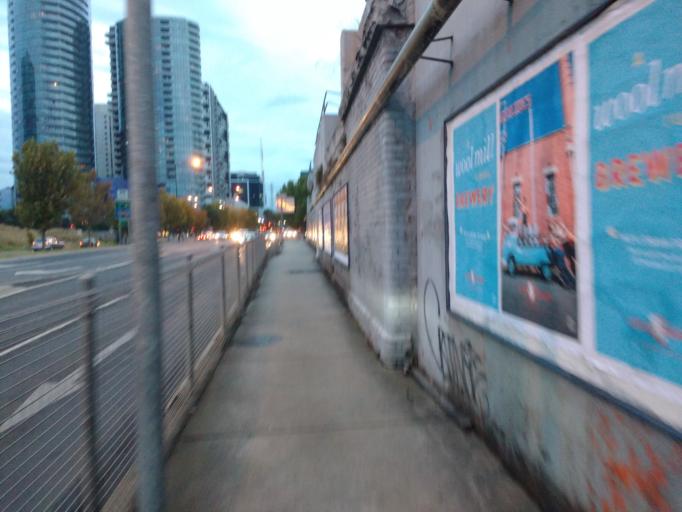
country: AU
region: Victoria
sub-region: Melbourne
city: West Melbourne
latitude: -37.8118
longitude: 144.9452
